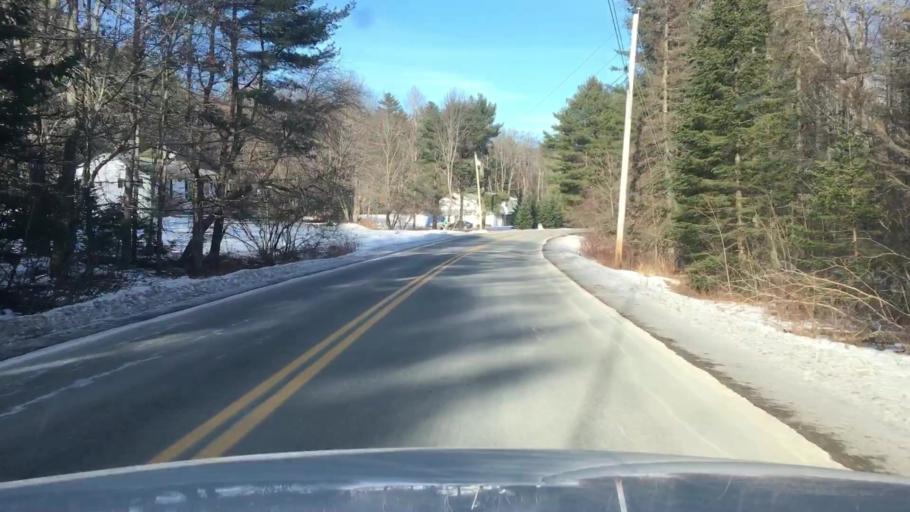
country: US
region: Maine
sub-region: Hancock County
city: Dedham
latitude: 44.6386
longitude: -68.6993
